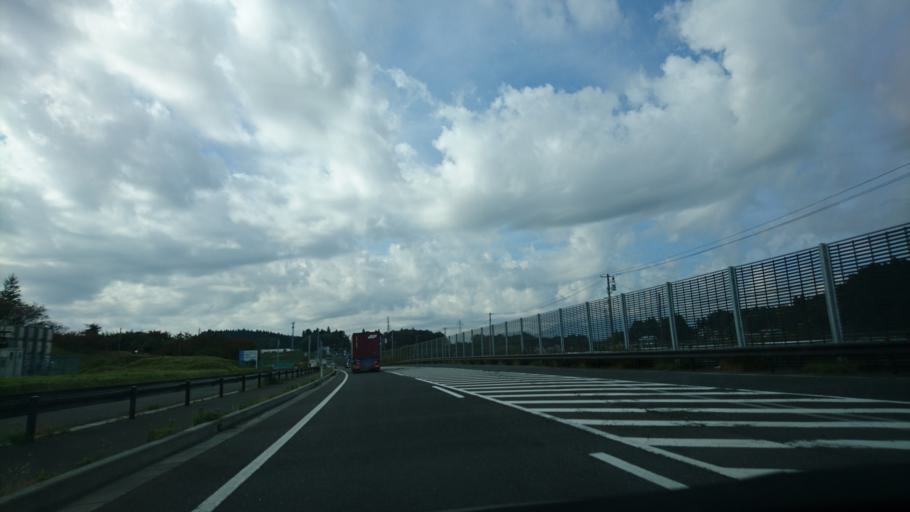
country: JP
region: Miyagi
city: Furukawa
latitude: 38.5107
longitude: 140.8949
